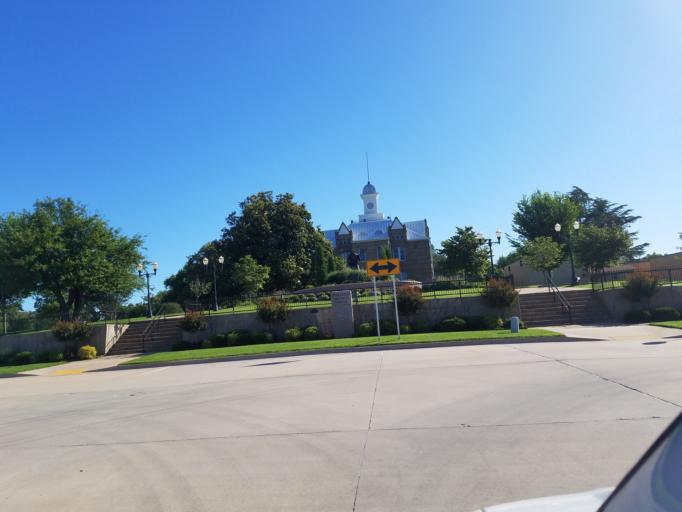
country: US
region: Oklahoma
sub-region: Johnston County
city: Tishomingo
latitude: 34.2561
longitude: -96.6711
